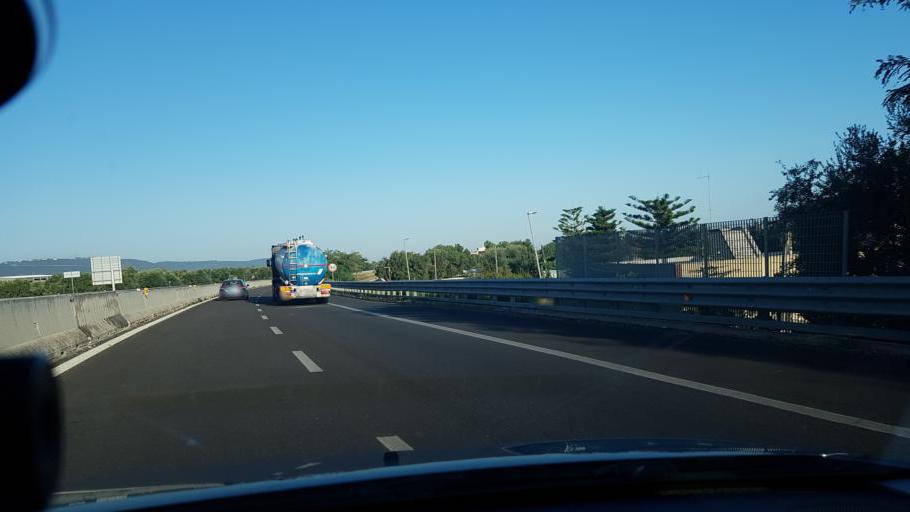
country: IT
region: Apulia
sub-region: Provincia di Brindisi
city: Fasano
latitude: 40.8422
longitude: 17.3674
